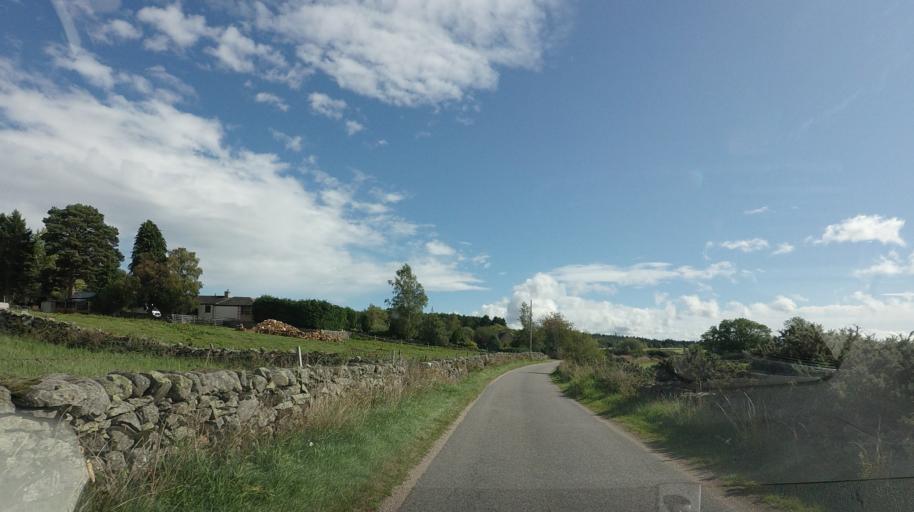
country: GB
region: Scotland
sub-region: Aberdeenshire
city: Banchory
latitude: 57.0656
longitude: -2.4719
